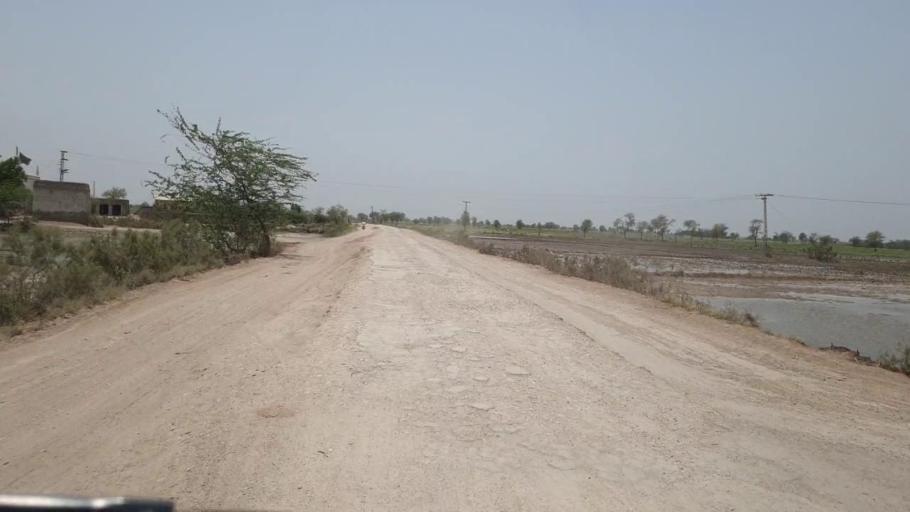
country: PK
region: Sindh
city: Daulatpur
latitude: 26.4623
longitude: 68.1409
